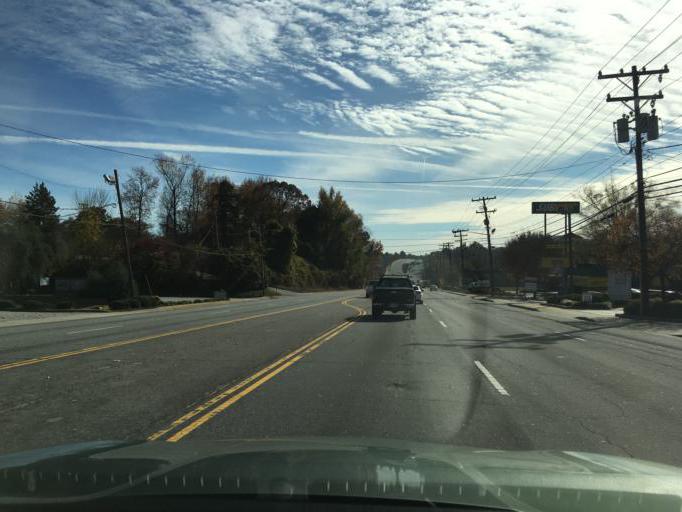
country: US
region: South Carolina
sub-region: Greenville County
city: Greenville
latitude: 34.8660
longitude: -82.3577
